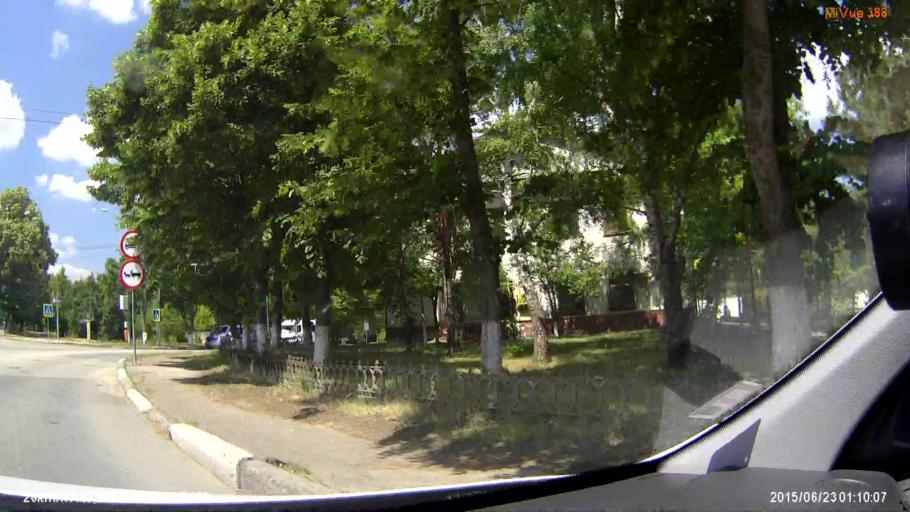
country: MD
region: Ungheni
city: Ungheni
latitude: 47.2016
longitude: 27.7955
